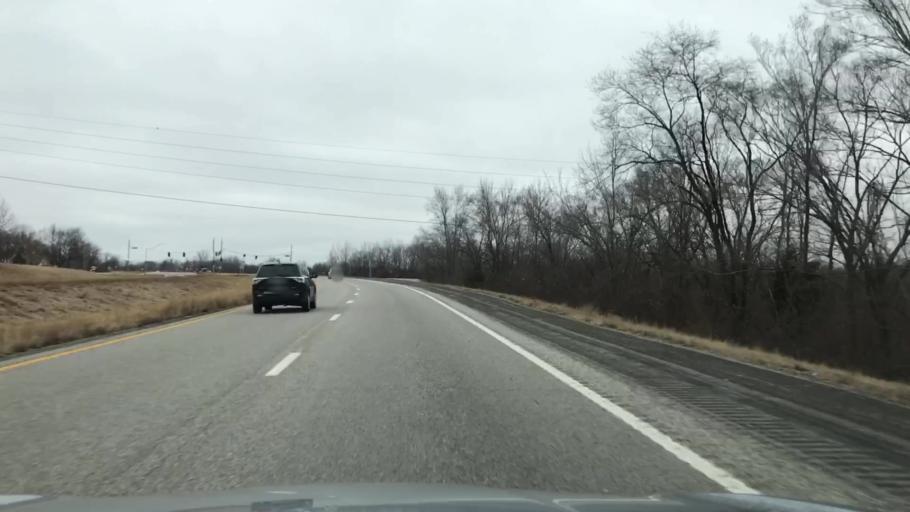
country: US
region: Missouri
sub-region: Clay County
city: Liberty
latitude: 39.2283
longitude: -94.4123
